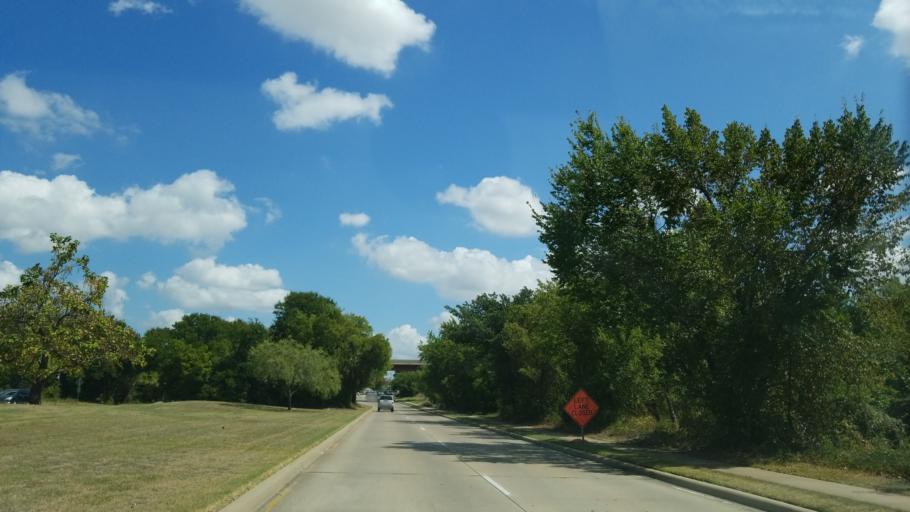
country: US
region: Texas
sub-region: Tarrant County
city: Grapevine
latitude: 32.9219
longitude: -97.0946
